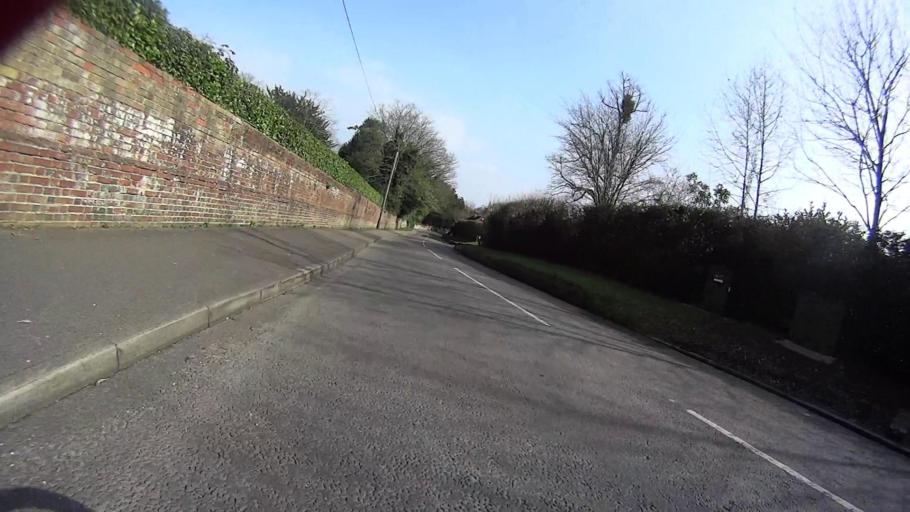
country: GB
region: England
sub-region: Surrey
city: Headley
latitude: 51.2408
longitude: -0.2683
